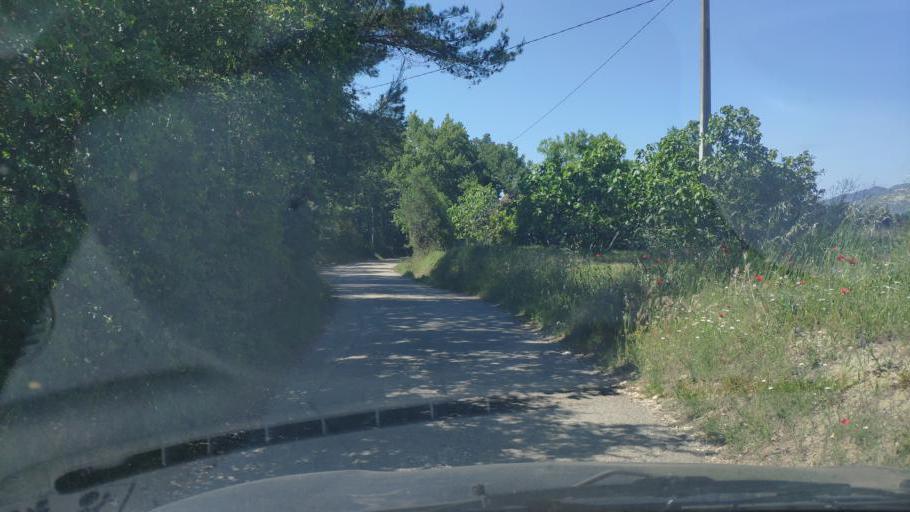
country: FR
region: Provence-Alpes-Cote d'Azur
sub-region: Departement du Vaucluse
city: Loriol-du-Comtat
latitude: 44.0737
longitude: 5.0137
